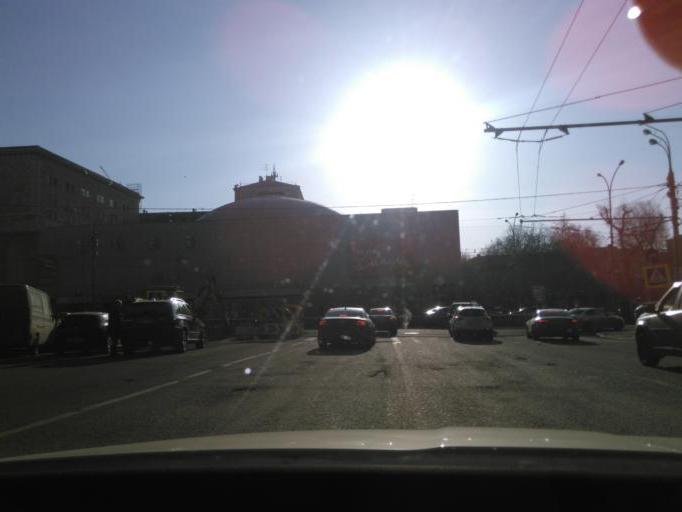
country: RU
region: Moscow
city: Moscow
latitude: 55.7689
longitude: 37.5939
